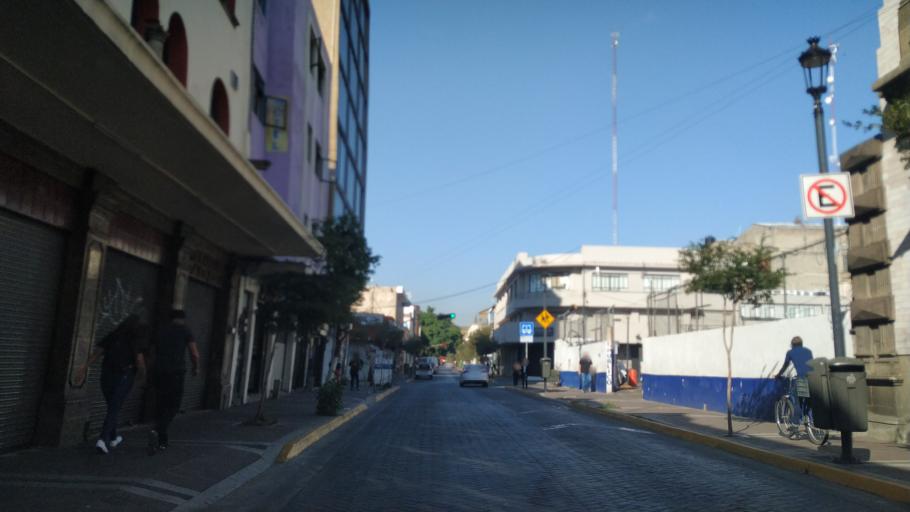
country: MX
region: Jalisco
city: Guadalajara
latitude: 20.6735
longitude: -103.3491
